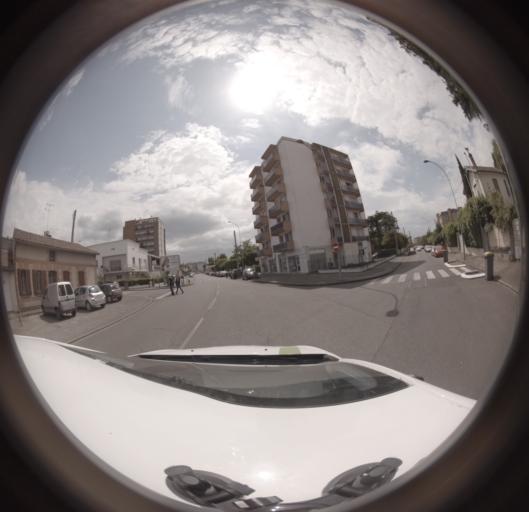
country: FR
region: Midi-Pyrenees
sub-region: Departement du Tarn-et-Garonne
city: Montauban
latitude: 44.0170
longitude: 1.3681
